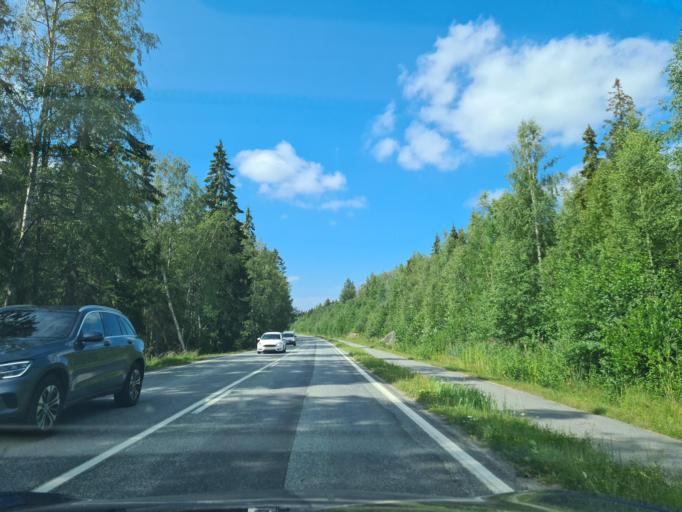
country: FI
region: Ostrobothnia
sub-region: Vaasa
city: Vaasa
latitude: 63.1965
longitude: 21.5445
